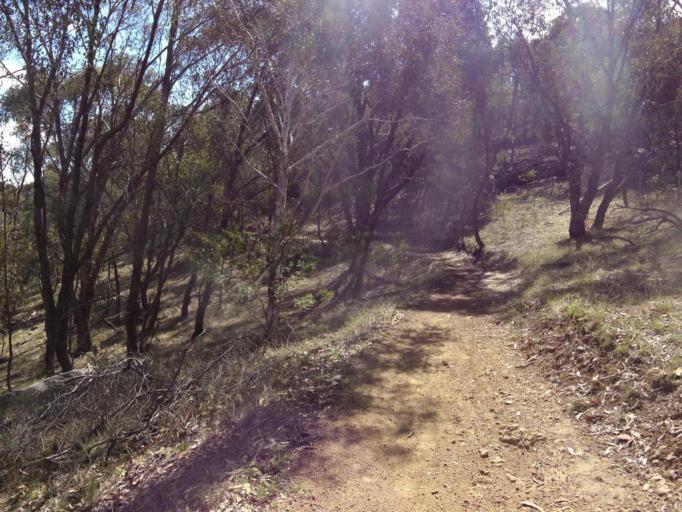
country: AU
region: Australian Capital Territory
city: Belconnen
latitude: -35.1538
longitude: 149.0854
